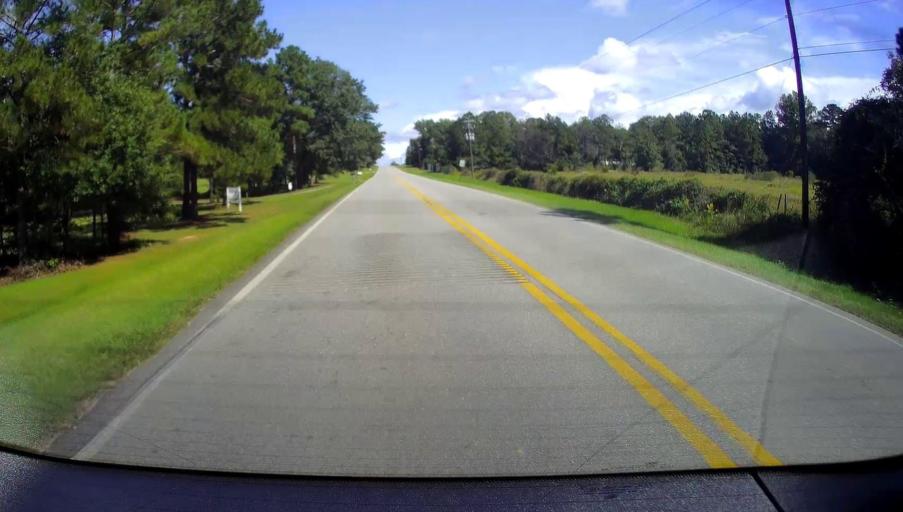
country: US
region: Georgia
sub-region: Houston County
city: Warner Robins
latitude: 32.7099
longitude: -83.5437
